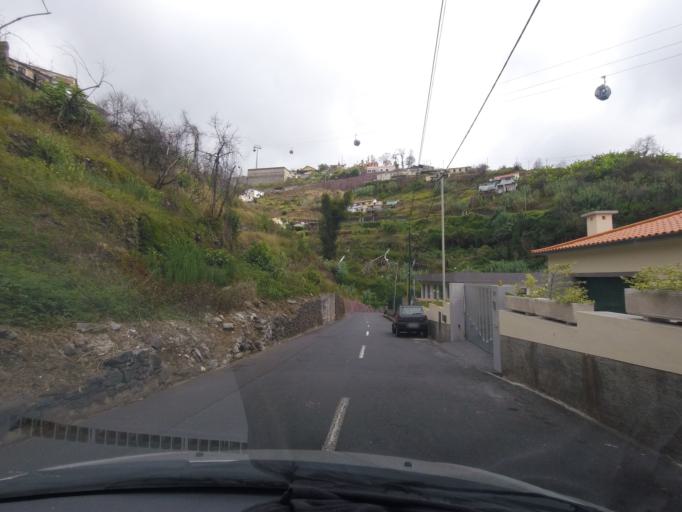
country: PT
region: Madeira
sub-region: Funchal
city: Nossa Senhora do Monte
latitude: 32.6672
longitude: -16.9016
